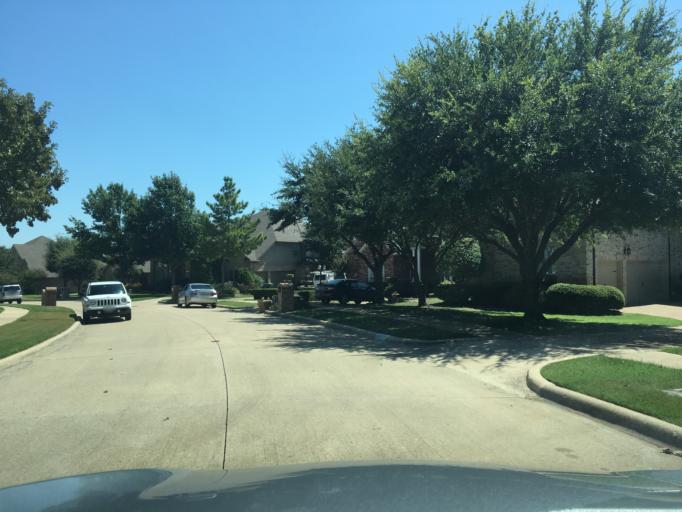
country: US
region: Texas
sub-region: Dallas County
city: Sachse
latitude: 32.9580
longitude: -96.6233
